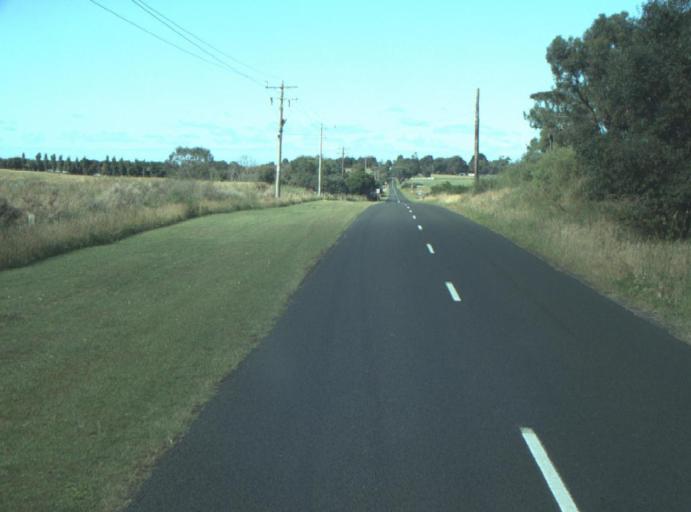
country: AU
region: Victoria
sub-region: Greater Geelong
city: Clifton Springs
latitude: -38.2271
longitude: 144.5850
